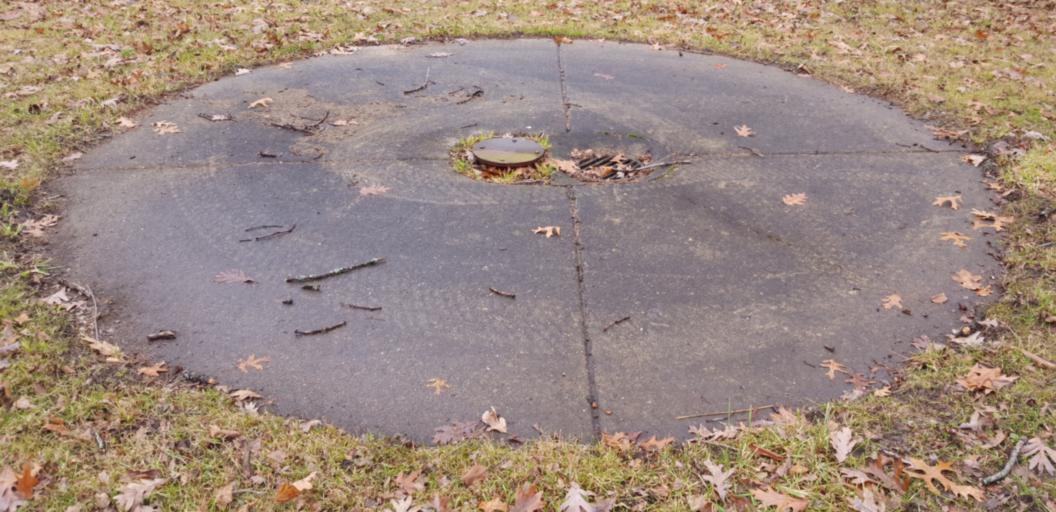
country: US
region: Illinois
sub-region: Cook County
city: Northbrook
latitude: 42.1393
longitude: -87.8233
